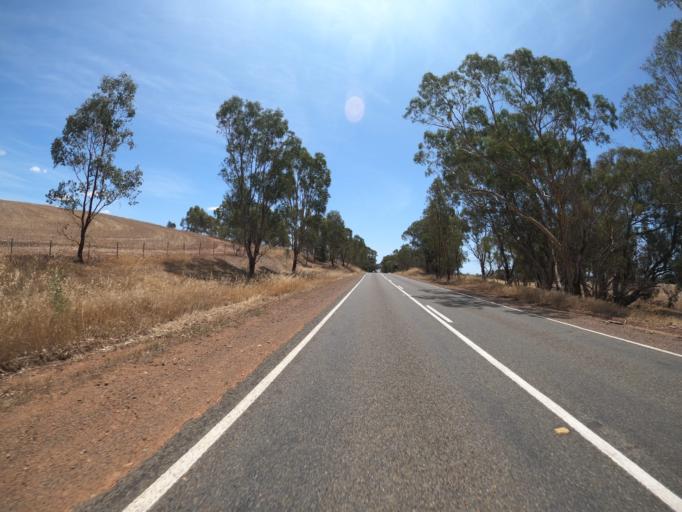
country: AU
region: Victoria
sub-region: Benalla
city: Benalla
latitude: -36.3265
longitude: 145.9602
